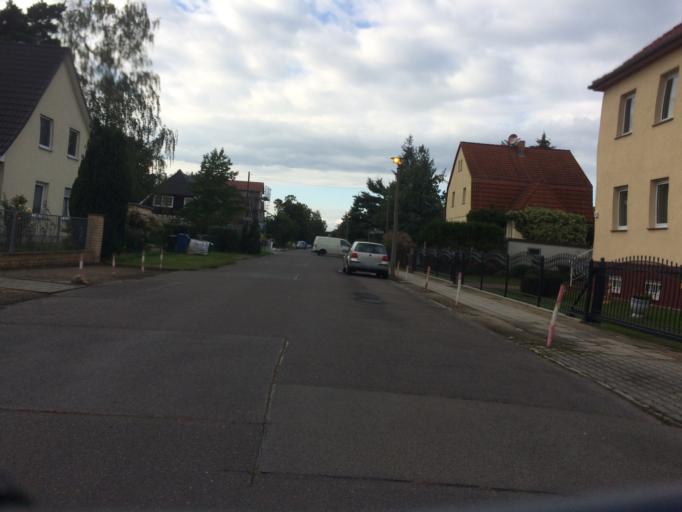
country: DE
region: Berlin
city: Karow
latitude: 52.6078
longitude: 13.4711
